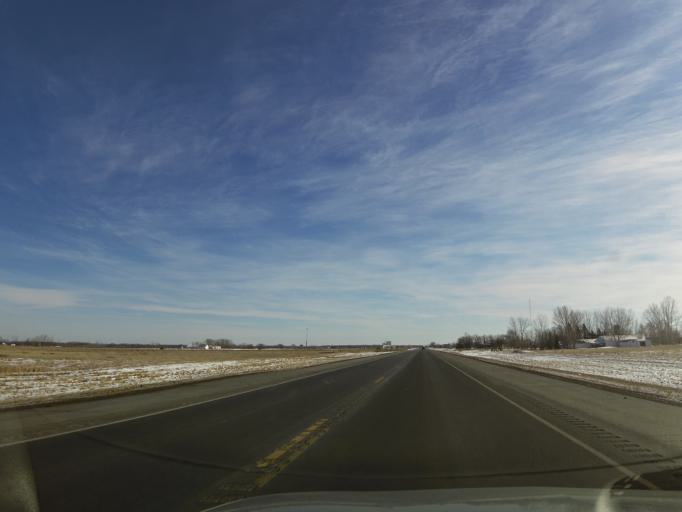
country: US
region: North Dakota
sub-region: Walsh County
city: Grafton
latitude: 48.4126
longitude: -97.4620
